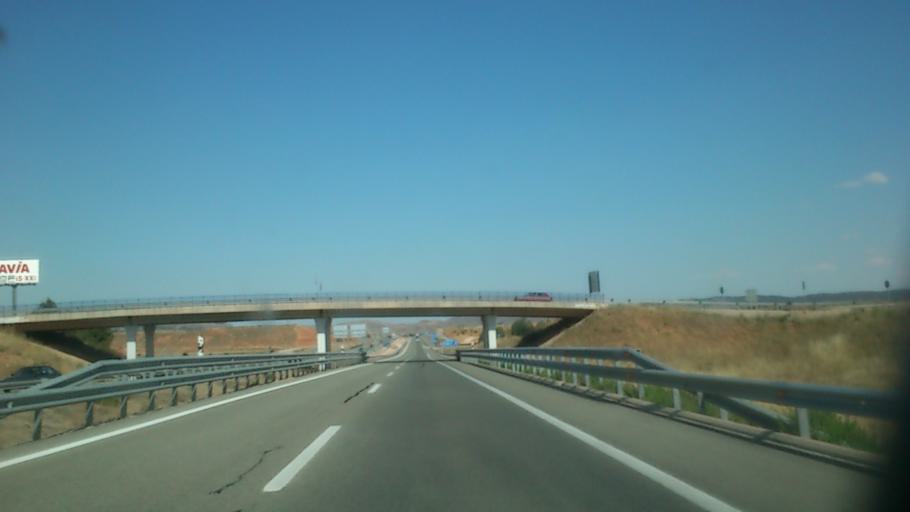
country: ES
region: Aragon
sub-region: Provincia de Zaragoza
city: Cetina
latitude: 41.3051
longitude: -1.9666
